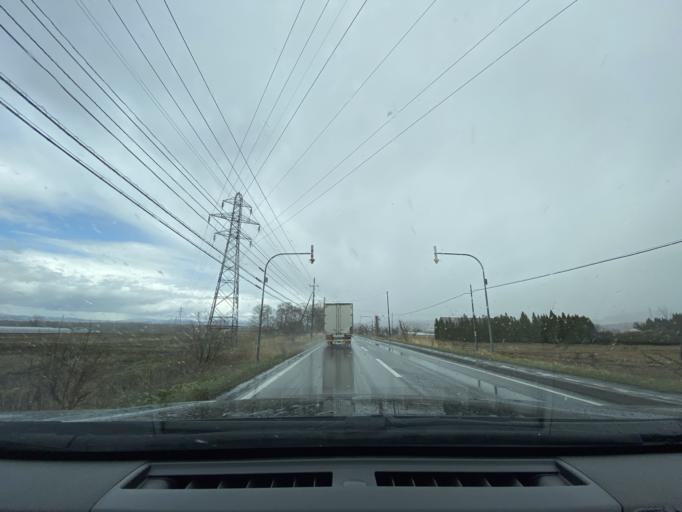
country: JP
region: Hokkaido
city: Fukagawa
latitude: 43.6650
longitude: 142.0017
